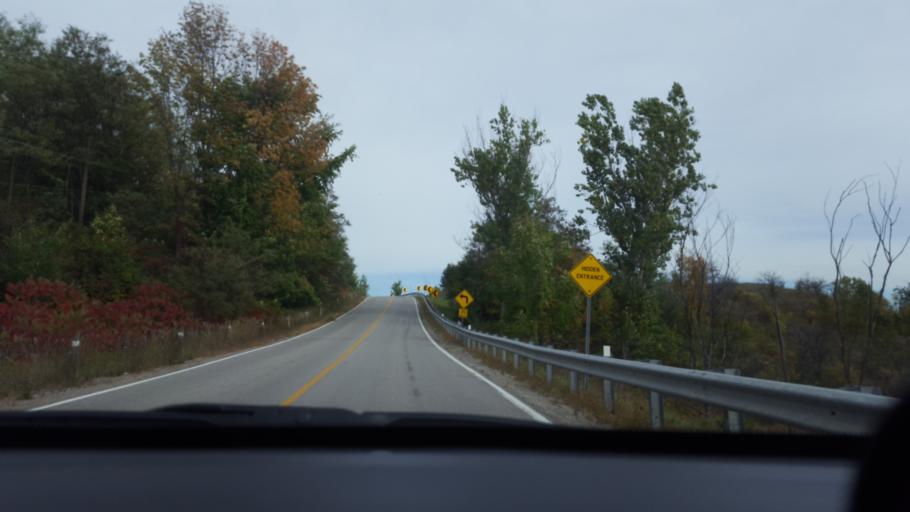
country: CA
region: Ontario
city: Newmarket
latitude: 44.0284
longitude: -79.5540
